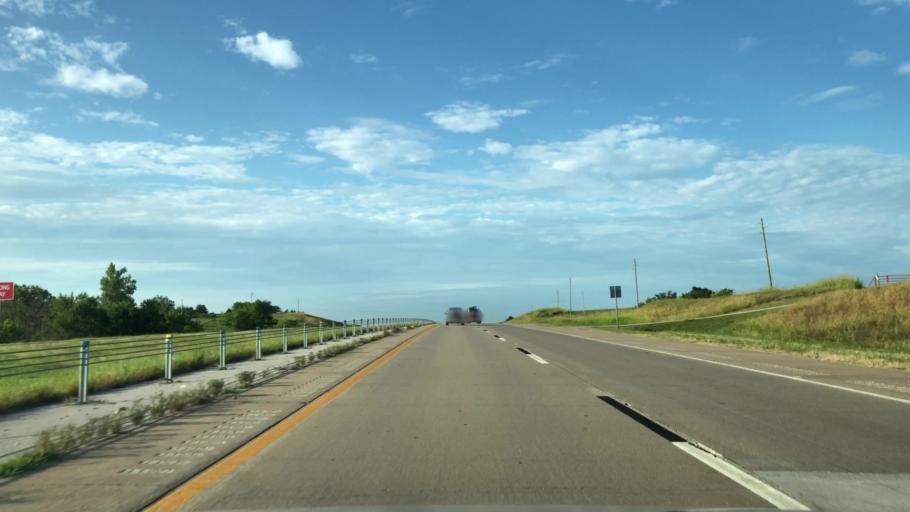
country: US
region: Oklahoma
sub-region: Osage County
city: Skiatook
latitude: 36.4813
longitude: -95.9207
